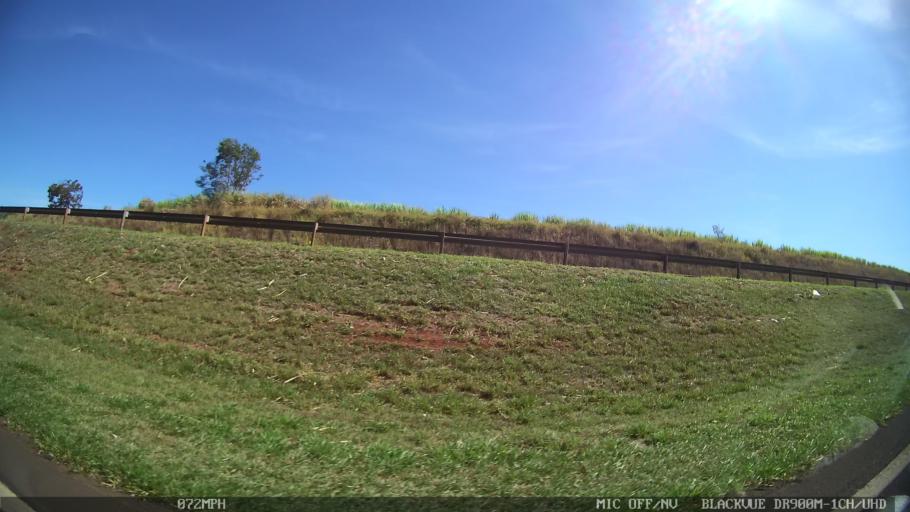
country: BR
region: Sao Paulo
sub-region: Sao Simao
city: Sao Simao
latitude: -21.4987
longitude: -47.6417
